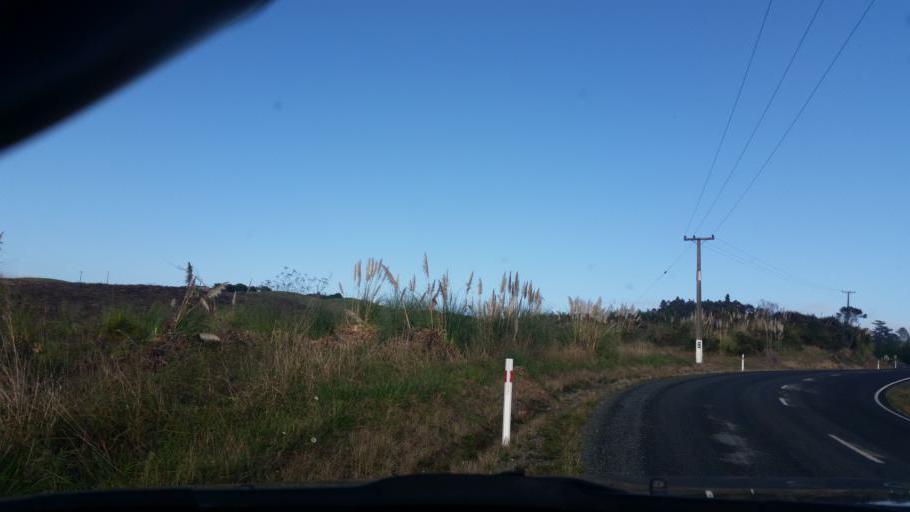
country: NZ
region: Auckland
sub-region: Auckland
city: Wellsford
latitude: -36.2199
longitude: 174.4634
